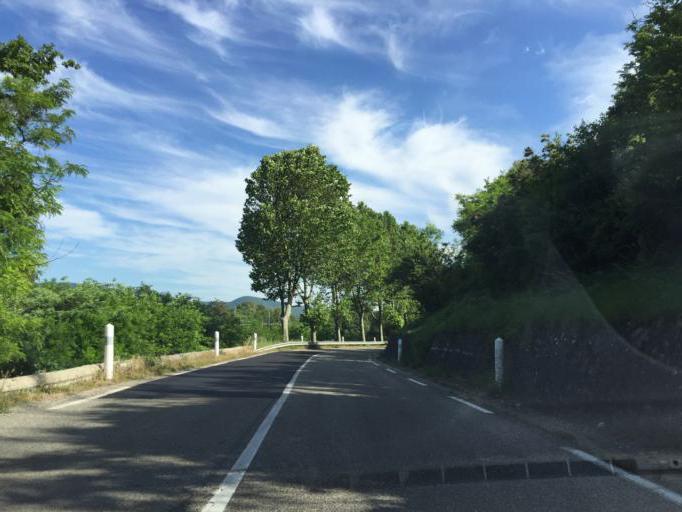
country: FR
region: Rhone-Alpes
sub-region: Departement de la Drome
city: Saulce-sur-Rhone
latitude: 44.7040
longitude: 4.7651
